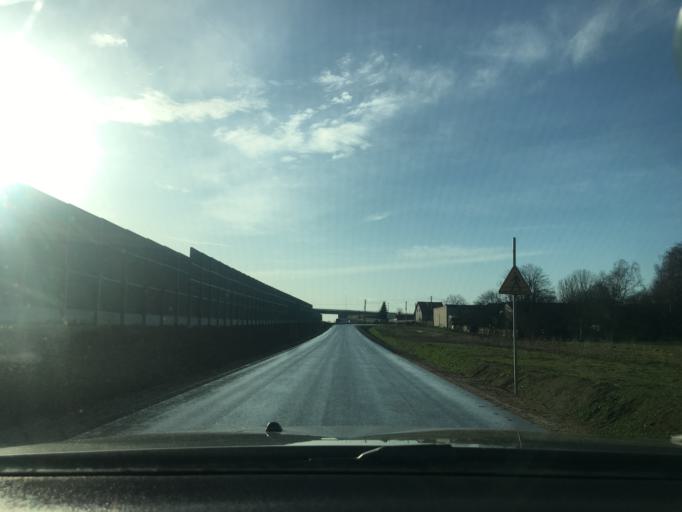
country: PL
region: Swietokrzyskie
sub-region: Powiat jedrzejowski
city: Jedrzejow
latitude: 50.6626
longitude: 20.3329
